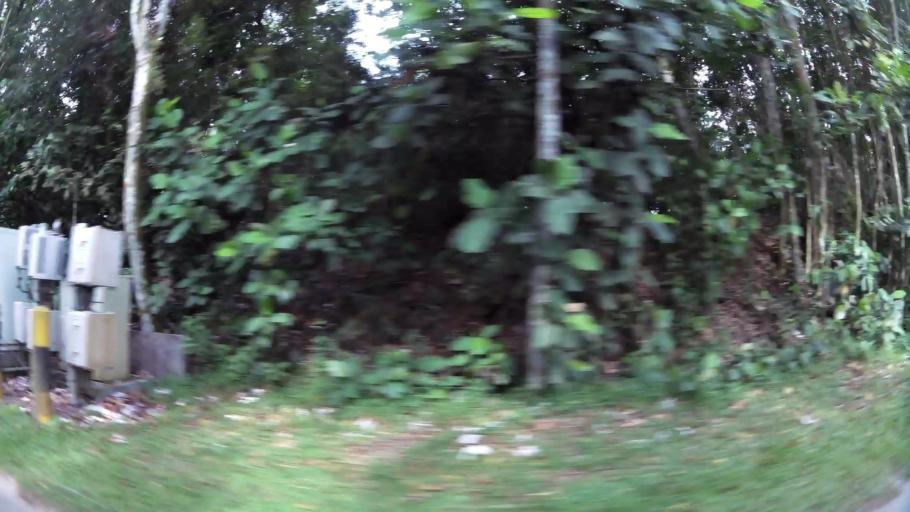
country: MY
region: Johor
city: Johor Bahru
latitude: 1.4085
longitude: 103.7013
